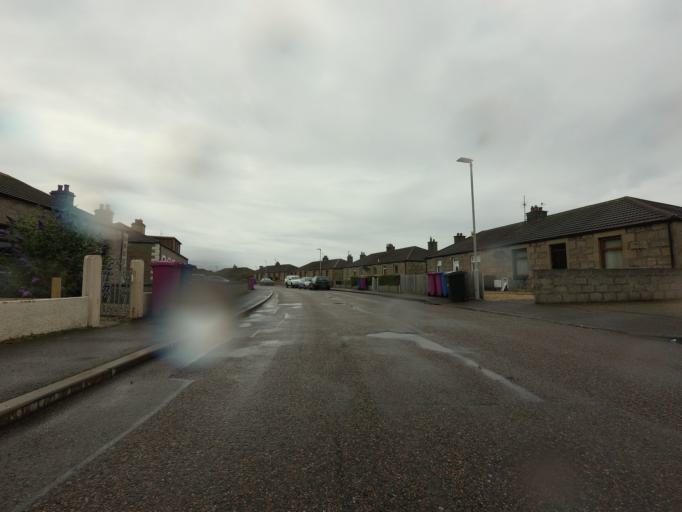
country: GB
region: Scotland
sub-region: Moray
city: Buckie
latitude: 57.6774
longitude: -2.9532
